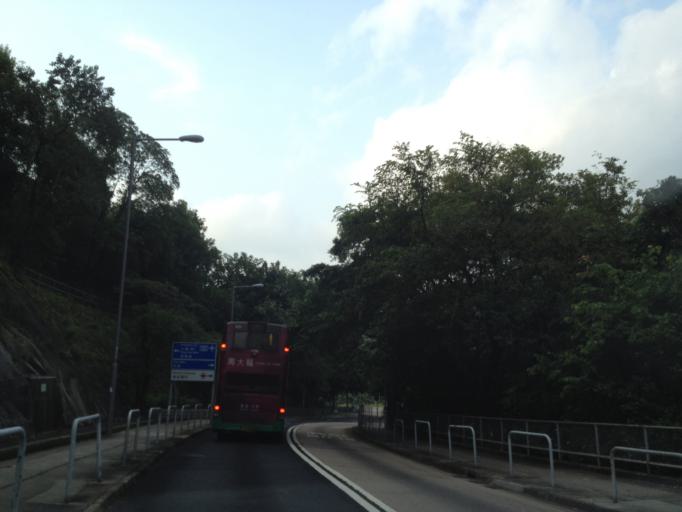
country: HK
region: Wanchai
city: Wan Chai
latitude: 22.2701
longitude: 114.2331
